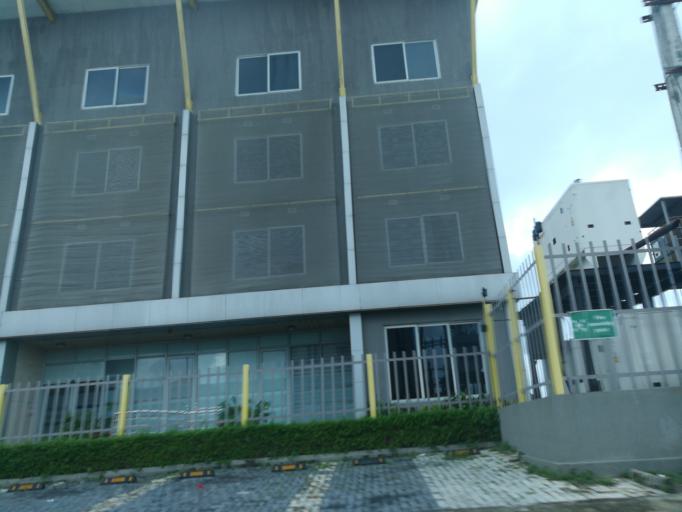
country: NG
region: Lagos
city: Ikoyi
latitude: 6.4389
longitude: 3.4728
